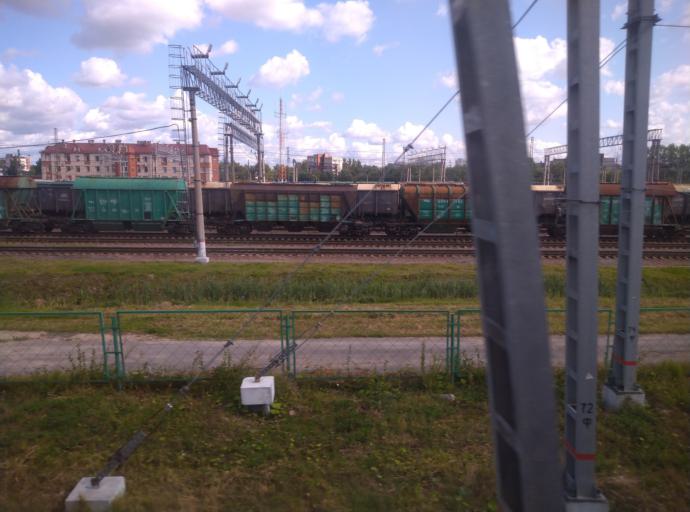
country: RU
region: St.-Petersburg
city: Obukhovo
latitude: 59.8621
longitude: 30.4328
